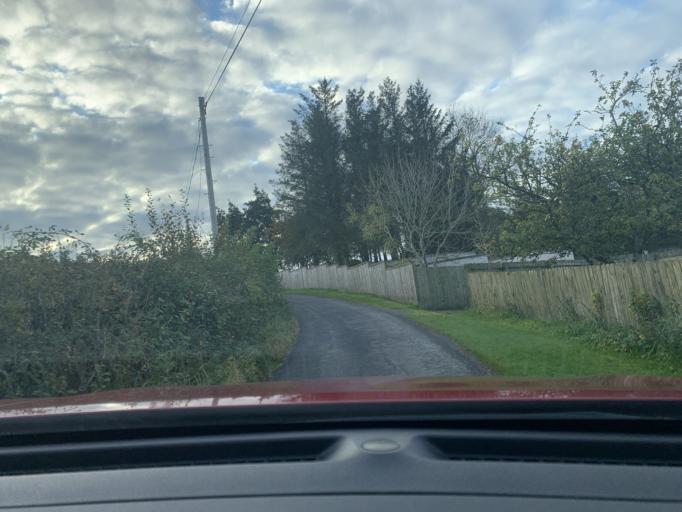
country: IE
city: Ballisodare
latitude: 54.2344
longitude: -8.5173
